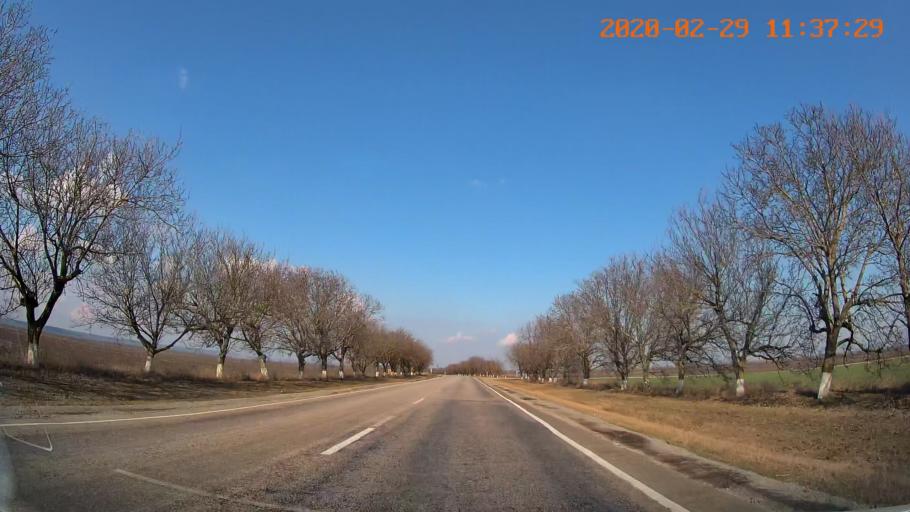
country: MD
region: Rezina
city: Saharna
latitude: 47.6123
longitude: 29.0457
